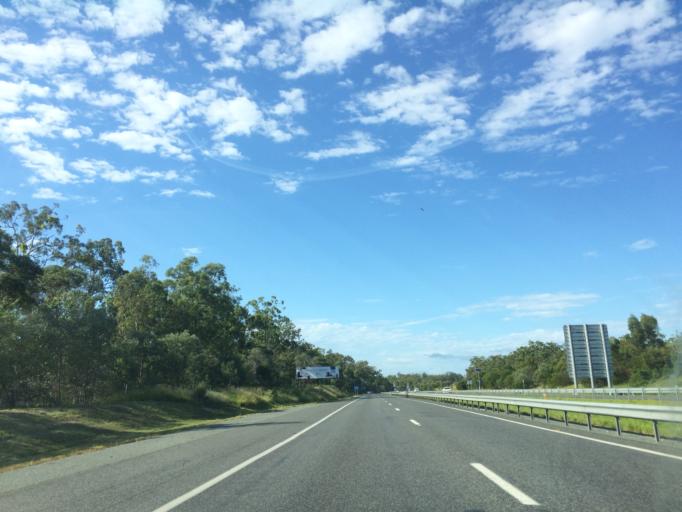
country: AU
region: Queensland
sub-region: Ipswich
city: Springfield
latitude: -27.6357
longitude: 152.9395
